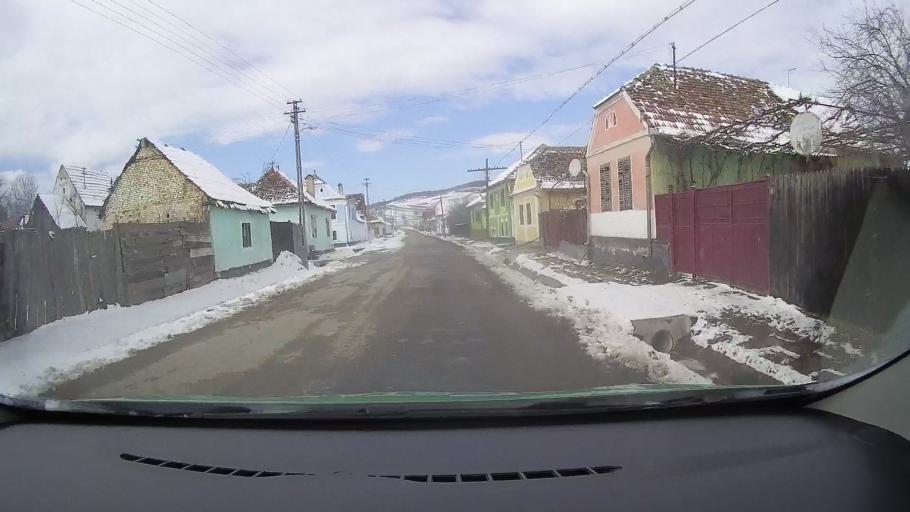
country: RO
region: Sibiu
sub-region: Comuna Altina
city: Altina
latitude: 45.9856
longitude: 24.4534
